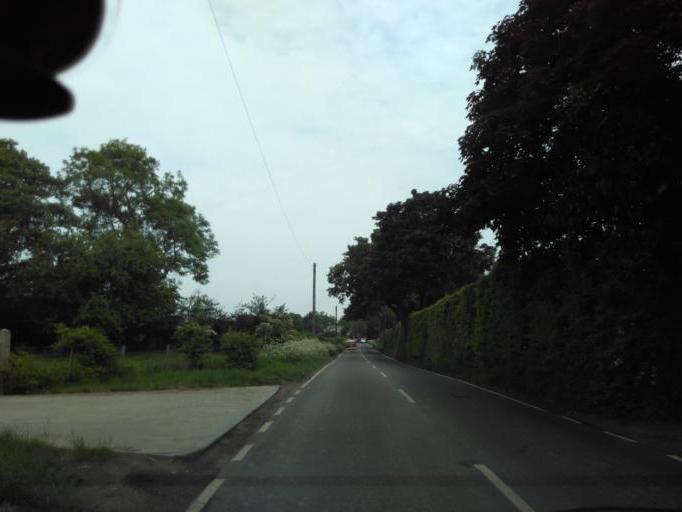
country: GB
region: England
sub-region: Kent
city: Chartham
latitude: 51.1956
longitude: 1.0561
